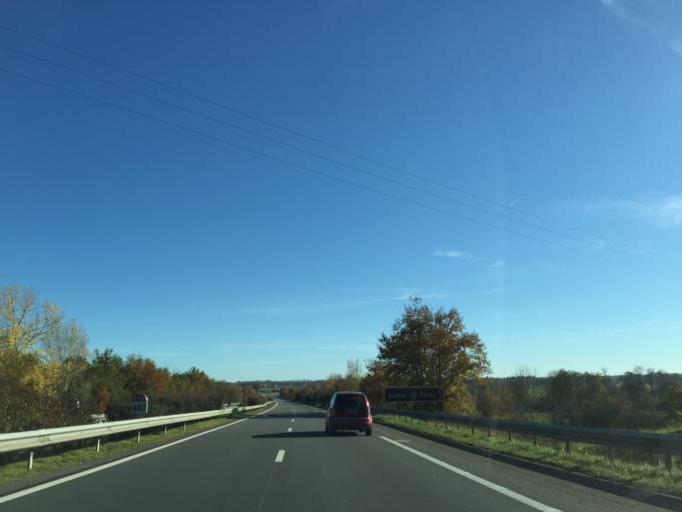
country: FR
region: Rhone-Alpes
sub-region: Departement de la Loire
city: Saint-Germain-Laval
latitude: 45.8312
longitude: 4.1007
